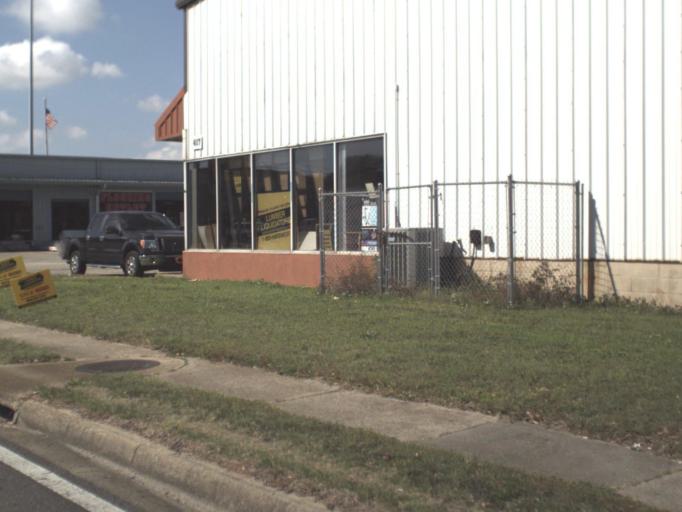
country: US
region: Florida
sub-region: Escambia County
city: Goulding
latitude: 30.4576
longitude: -87.2234
